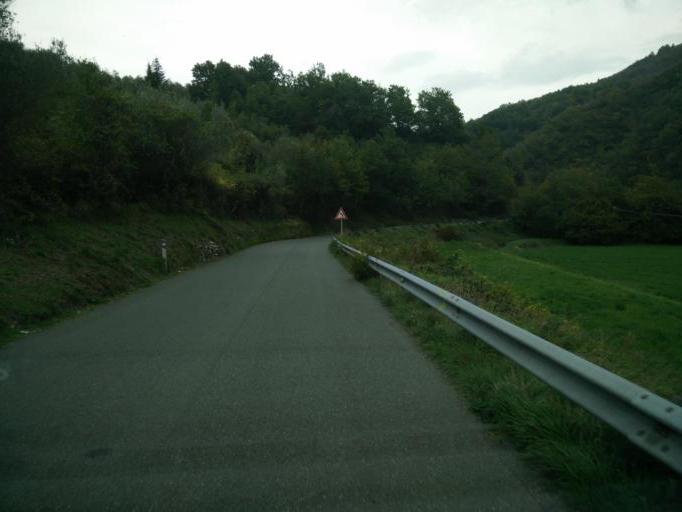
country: IT
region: Tuscany
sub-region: Provincia di Massa-Carrara
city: Casola in Lunigiana
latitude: 44.1939
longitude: 10.1522
